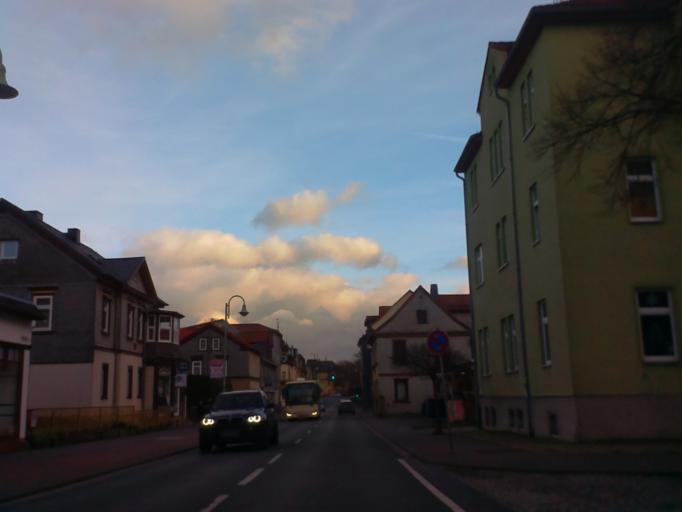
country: DE
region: Thuringia
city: Bad Blankenburg
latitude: 50.6838
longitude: 11.2678
